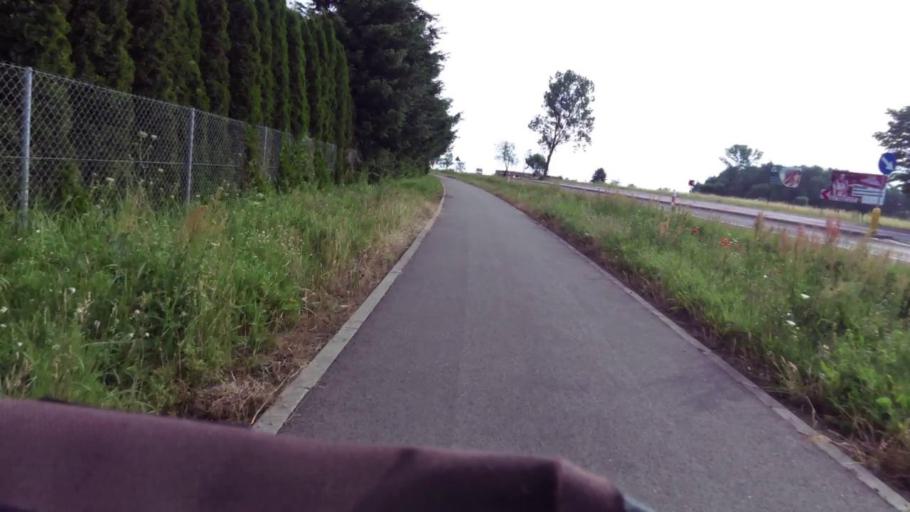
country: PL
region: West Pomeranian Voivodeship
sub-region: Powiat kamienski
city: Kamien Pomorski
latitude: 53.9797
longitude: 14.7946
